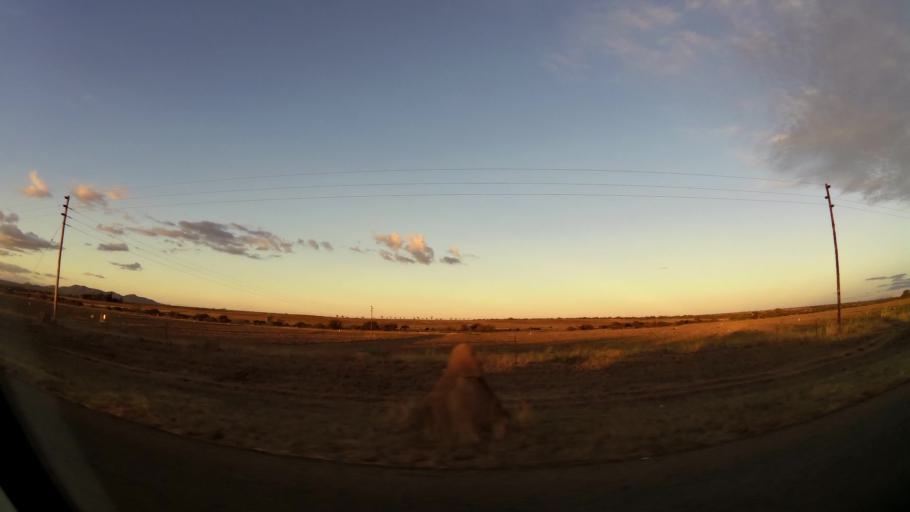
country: ZA
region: Limpopo
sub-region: Capricorn District Municipality
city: Polokwane
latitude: -23.7879
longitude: 29.4758
